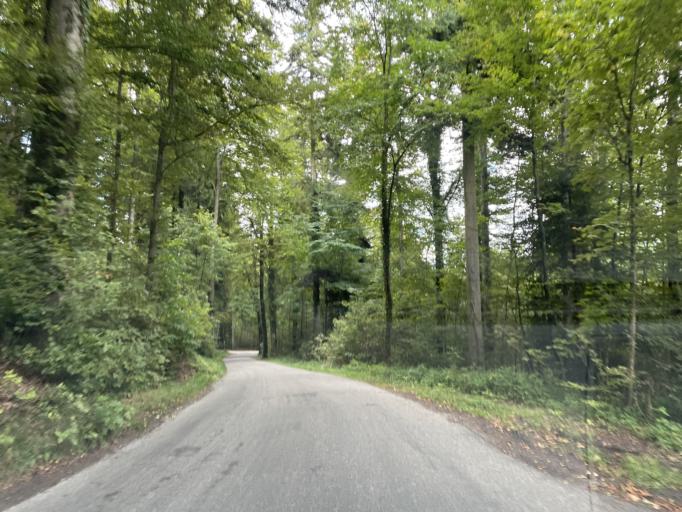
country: CH
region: Zurich
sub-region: Bezirk Winterthur
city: Seen (Kreis 3) / Waldegg
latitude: 47.4750
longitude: 8.7493
